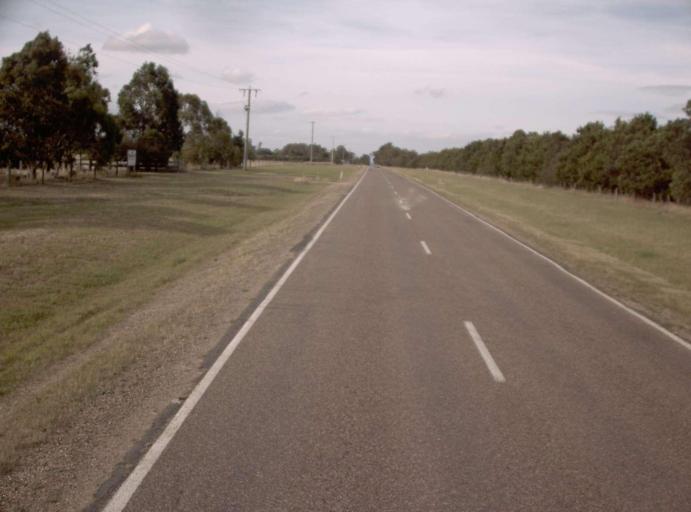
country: AU
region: Victoria
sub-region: Wellington
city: Heyfield
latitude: -38.0405
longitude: 146.6659
